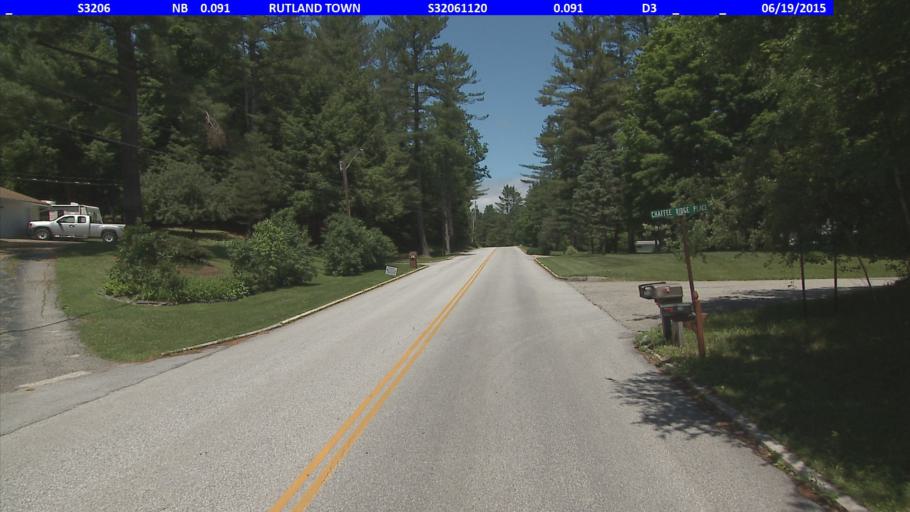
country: US
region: Vermont
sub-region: Rutland County
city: Rutland
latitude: 43.6312
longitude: -72.9887
